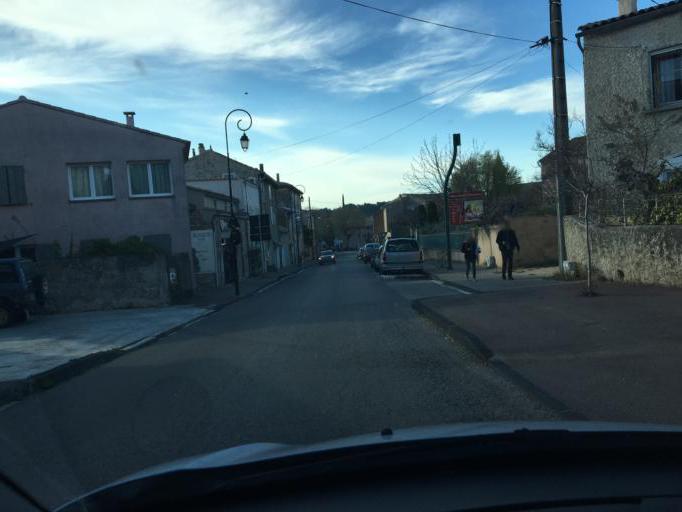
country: FR
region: Provence-Alpes-Cote d'Azur
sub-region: Departement du Vaucluse
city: Villes-sur-Auzon
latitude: 44.0569
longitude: 5.2367
